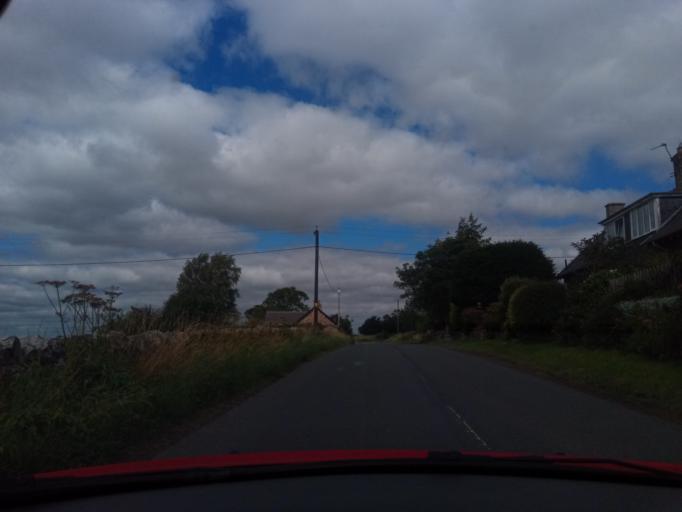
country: GB
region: Scotland
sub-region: The Scottish Borders
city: Kelso
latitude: 55.5307
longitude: -2.3594
